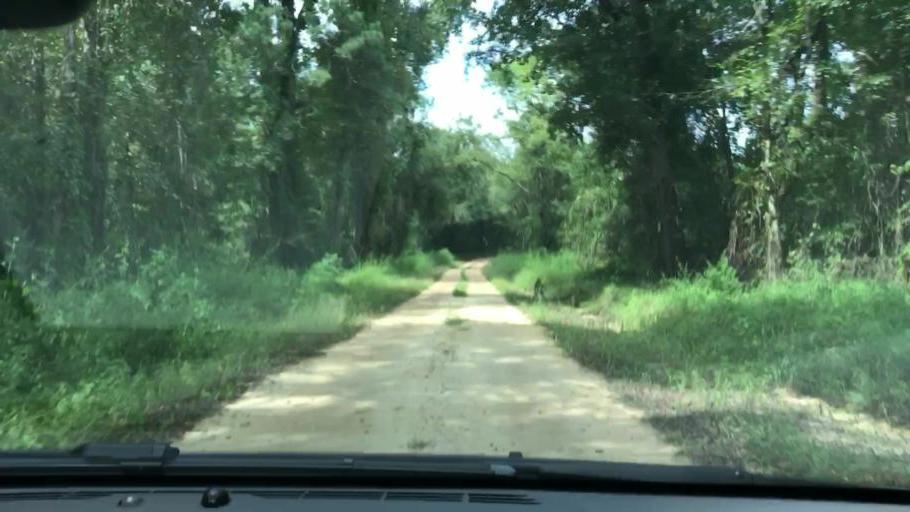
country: US
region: Georgia
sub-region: Quitman County
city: Georgetown
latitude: 32.0433
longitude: -85.0359
